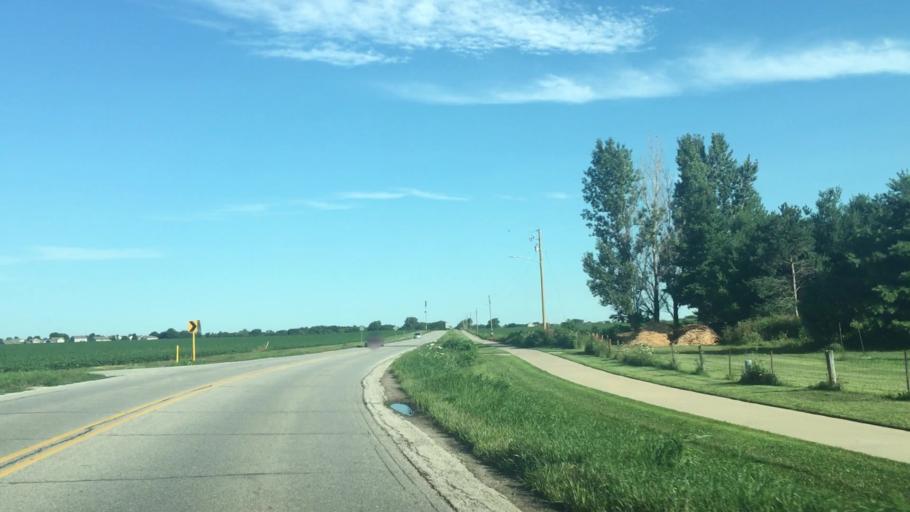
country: US
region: Iowa
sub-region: Johnson County
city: North Liberty
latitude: 41.7341
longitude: -91.5800
